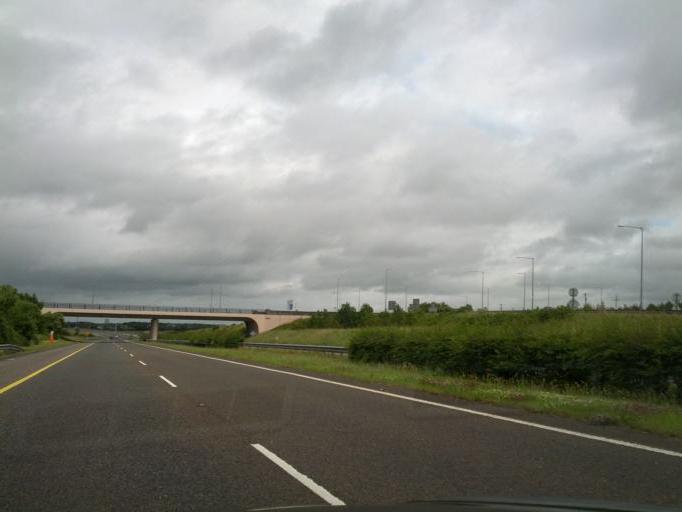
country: IE
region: Munster
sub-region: An Clar
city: Newmarket on Fergus
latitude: 52.7876
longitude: -8.9213
